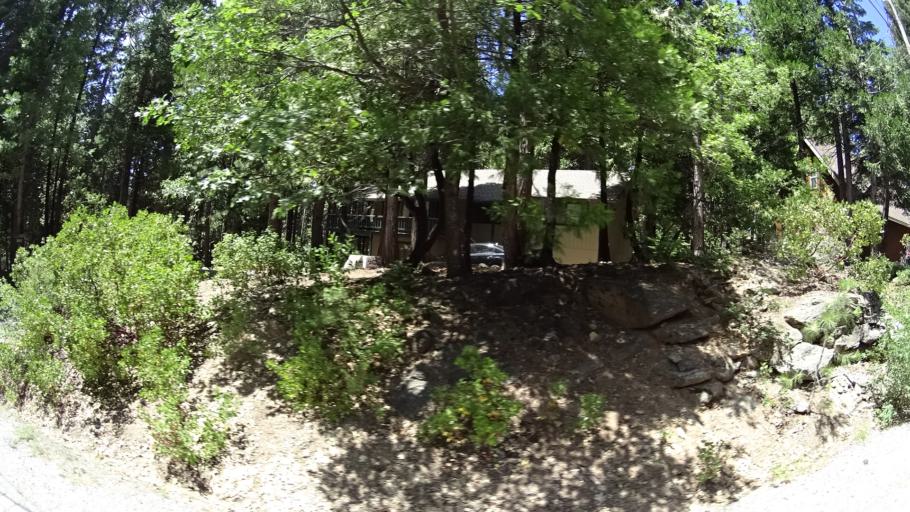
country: US
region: California
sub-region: Calaveras County
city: Arnold
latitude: 38.3043
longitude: -120.2704
